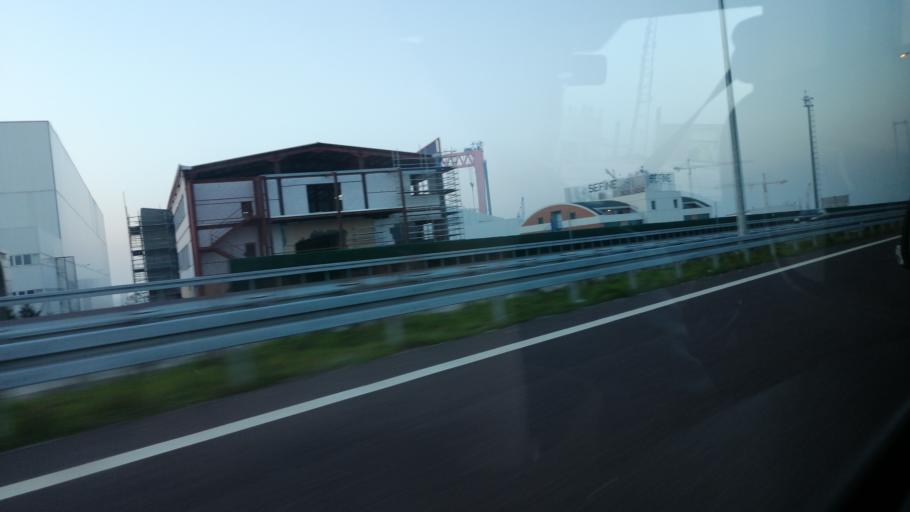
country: TR
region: Yalova
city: Altinova
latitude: 40.7273
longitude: 29.5049
